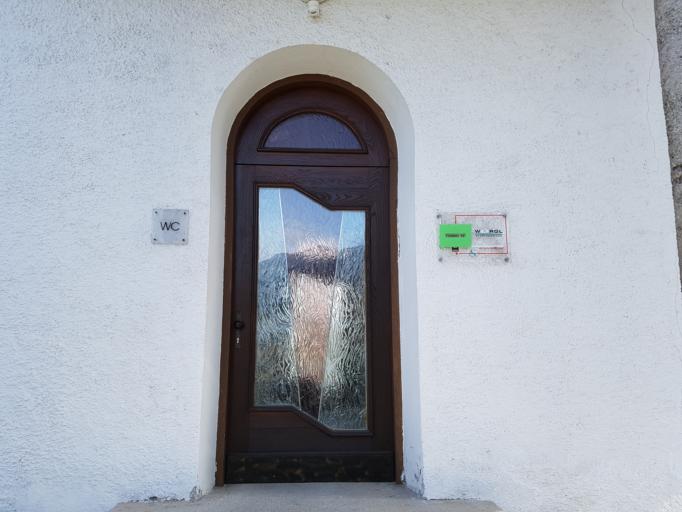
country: AT
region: Tyrol
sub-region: Politischer Bezirk Kufstein
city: Worgl
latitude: 47.4839
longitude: 12.0673
